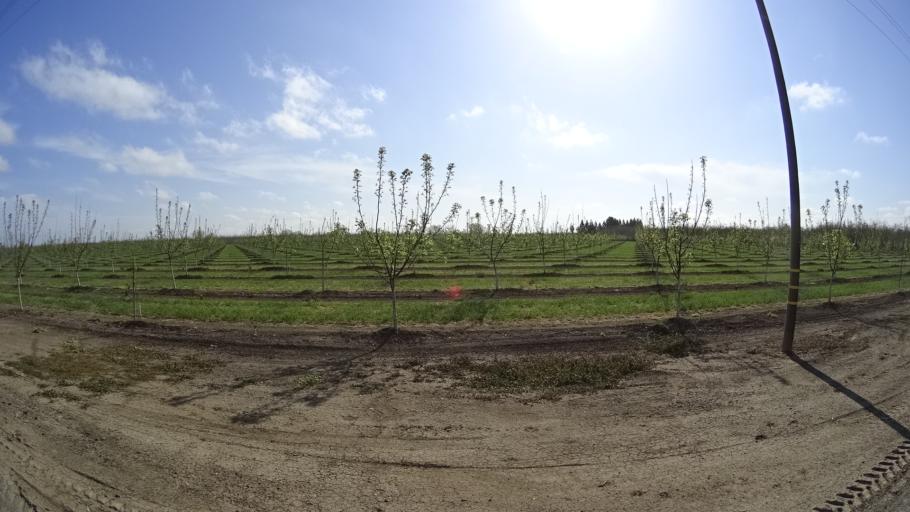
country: US
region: California
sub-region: Glenn County
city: Willows
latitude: 39.4707
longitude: -121.9678
